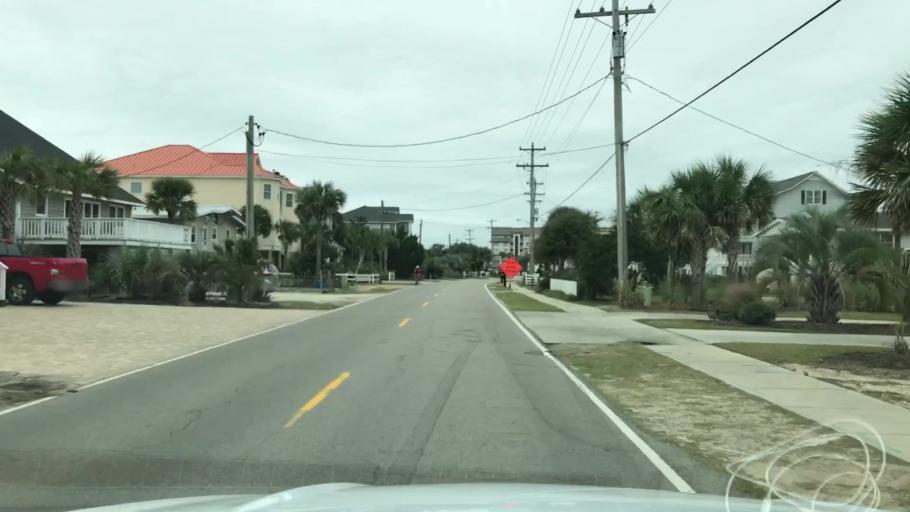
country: US
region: South Carolina
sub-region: Georgetown County
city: Murrells Inlet
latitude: 33.5552
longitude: -79.0167
